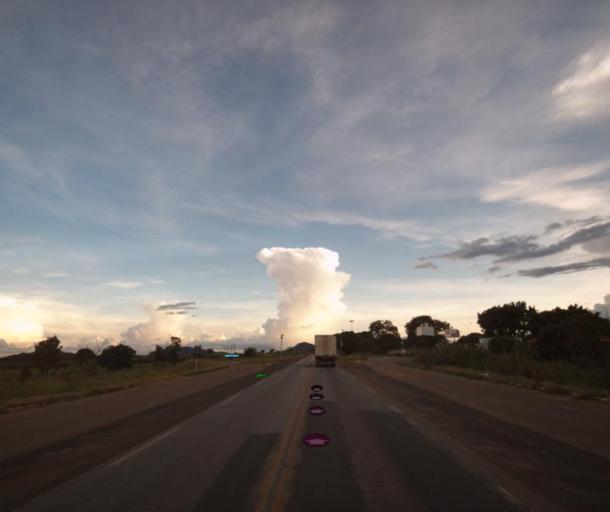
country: BR
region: Goias
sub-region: Uruacu
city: Uruacu
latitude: -14.3328
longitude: -49.1542
